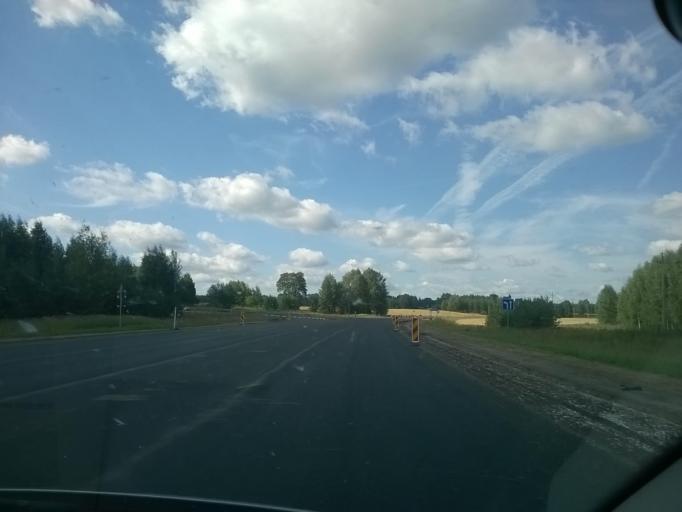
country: EE
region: Vorumaa
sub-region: Voru linn
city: Voru
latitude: 57.7951
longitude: 26.9551
